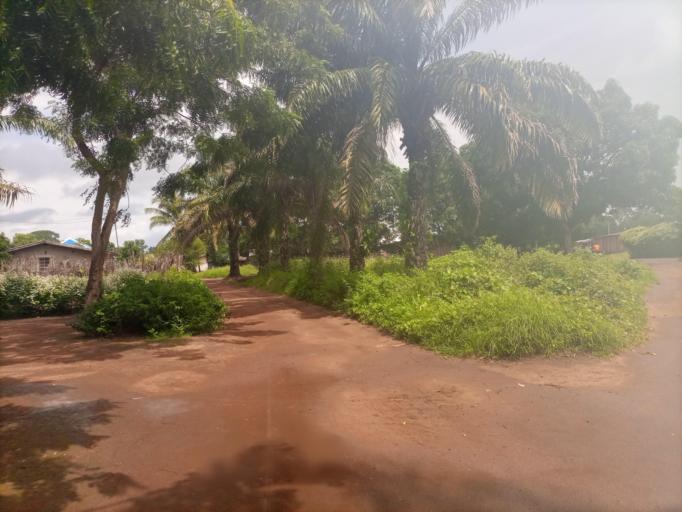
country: SL
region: Northern Province
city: Tintafor
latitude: 8.6330
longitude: -13.2166
